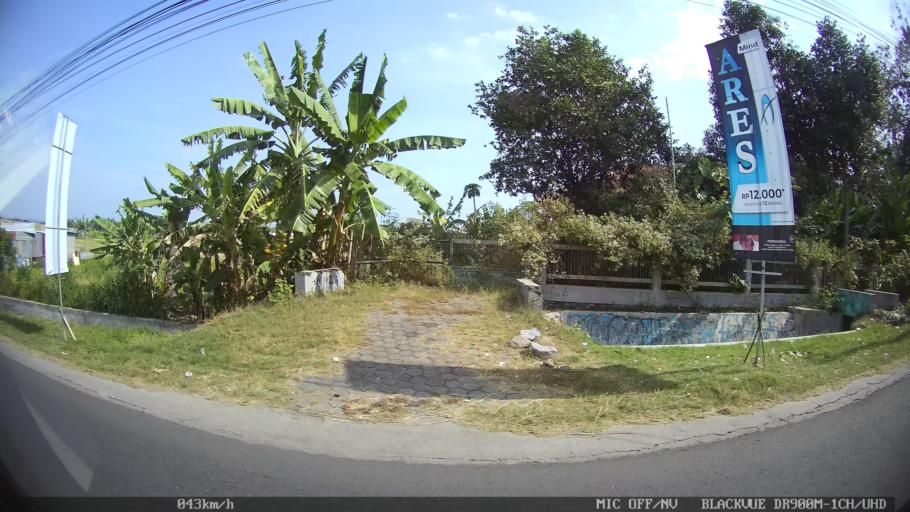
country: ID
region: Daerah Istimewa Yogyakarta
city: Kasihan
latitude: -7.8409
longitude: 110.3263
